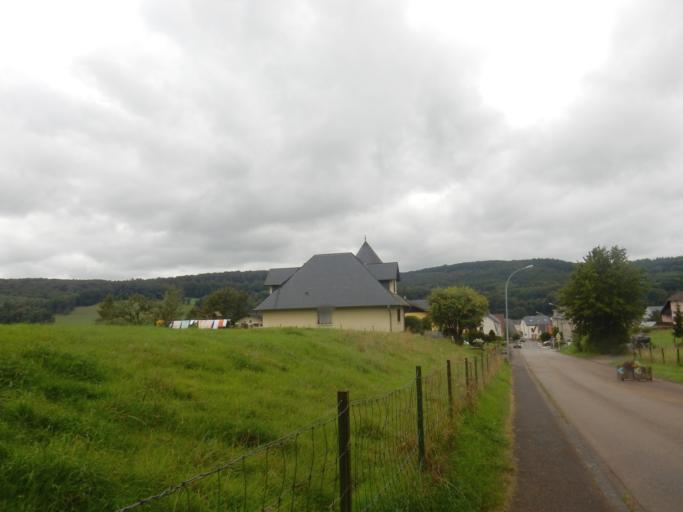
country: LU
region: Diekirch
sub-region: Canton de Diekirch
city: Schieren
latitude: 49.8326
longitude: 6.1006
